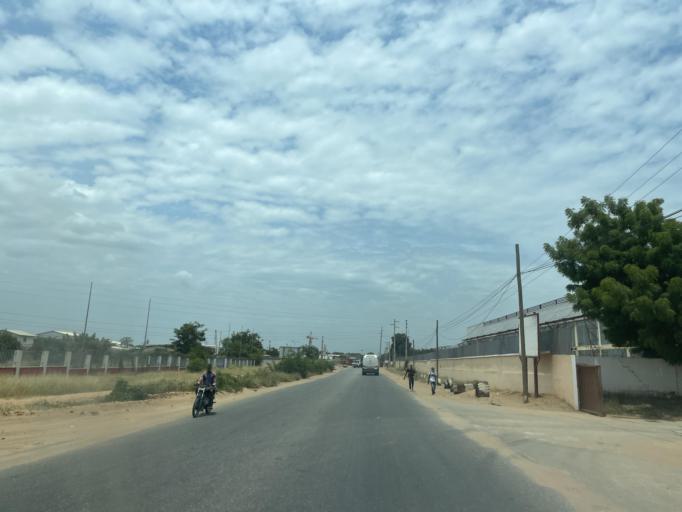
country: AO
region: Luanda
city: Luanda
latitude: -8.9347
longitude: 13.3914
